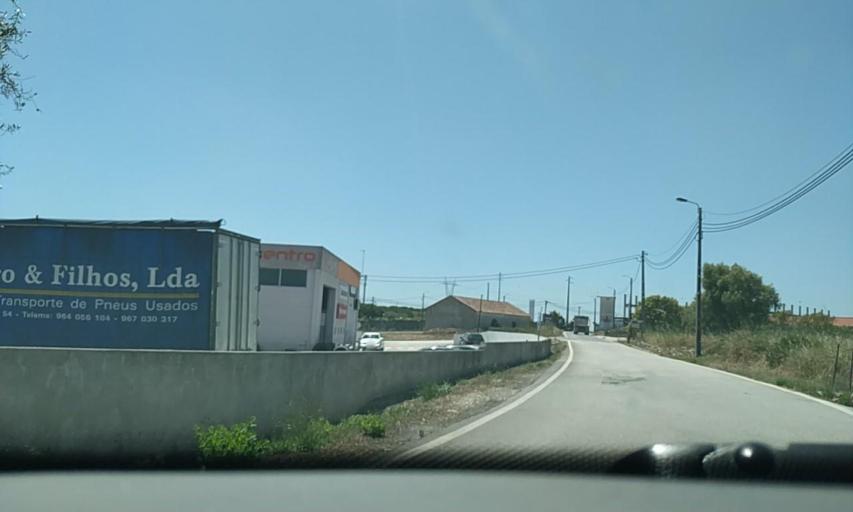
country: PT
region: Lisbon
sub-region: Sintra
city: Almargem
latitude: 38.8772
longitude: -9.2626
